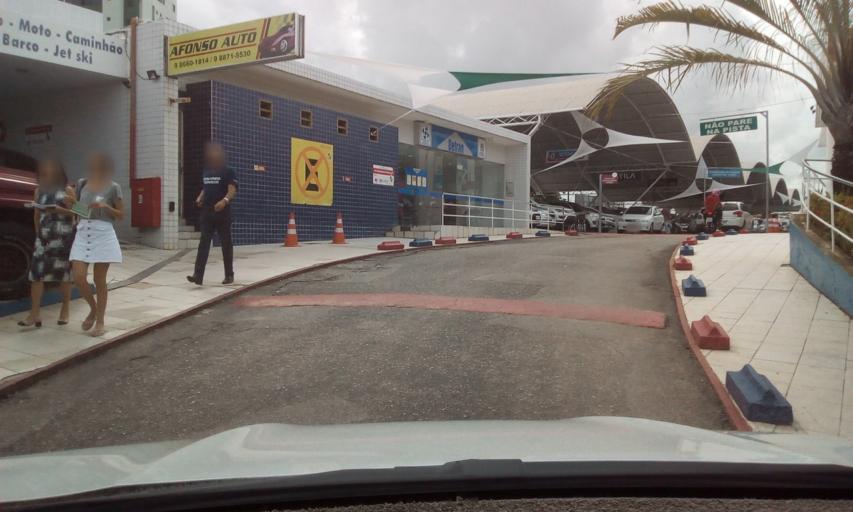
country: BR
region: Paraiba
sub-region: Joao Pessoa
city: Joao Pessoa
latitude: -7.0942
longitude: -34.8466
